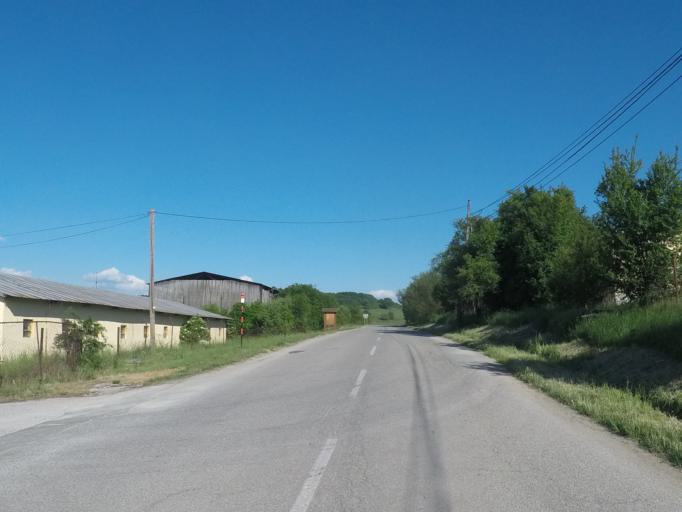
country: HU
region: Borsod-Abauj-Zemplen
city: Putnok
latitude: 48.4900
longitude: 20.4439
